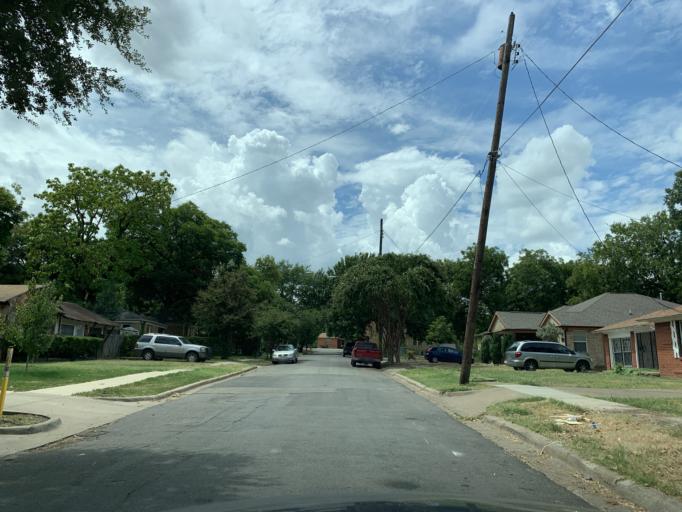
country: US
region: Texas
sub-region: Dallas County
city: Cockrell Hill
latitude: 32.7378
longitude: -96.8783
